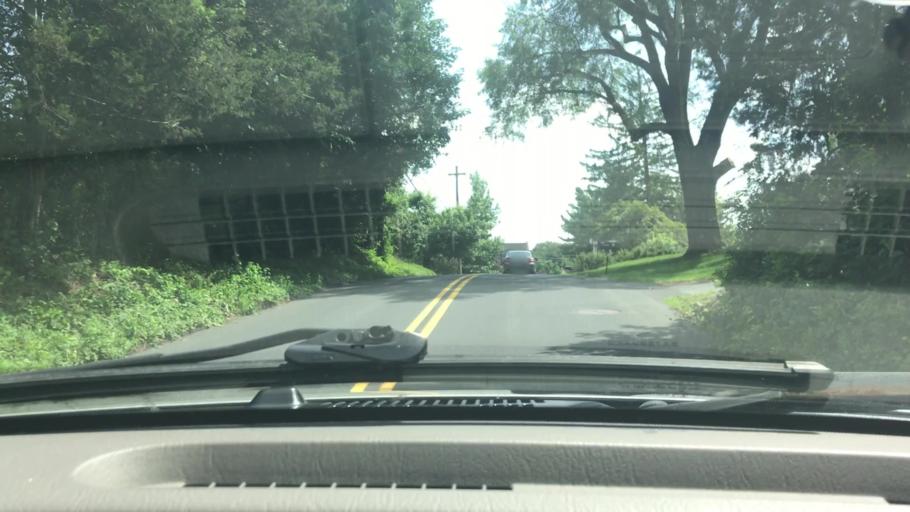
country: US
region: Pennsylvania
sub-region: Dauphin County
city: Paxtonia
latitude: 40.3198
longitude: -76.7909
